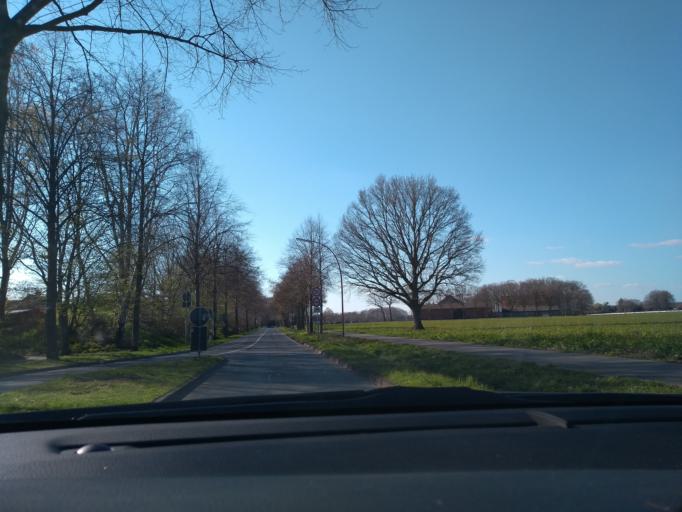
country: DE
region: North Rhine-Westphalia
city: Lunen
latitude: 51.6295
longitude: 7.4867
